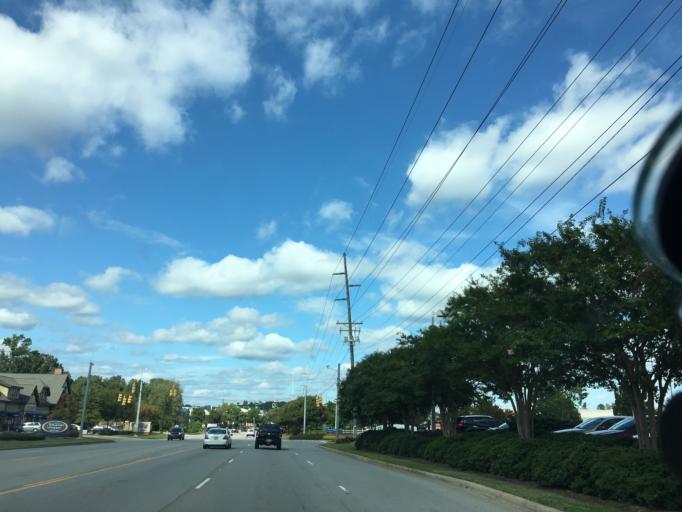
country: US
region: South Carolina
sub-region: Lexington County
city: Irmo
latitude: 34.0695
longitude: -81.1636
